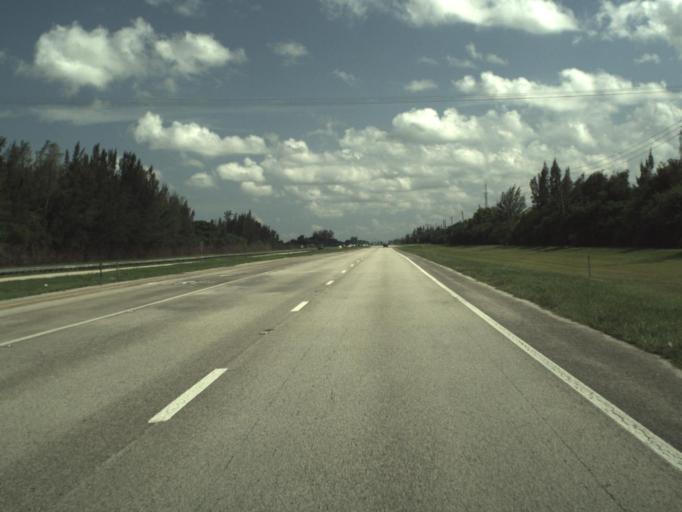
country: US
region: Florida
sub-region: Palm Beach County
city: Villages of Oriole
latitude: 26.4748
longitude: -80.2048
